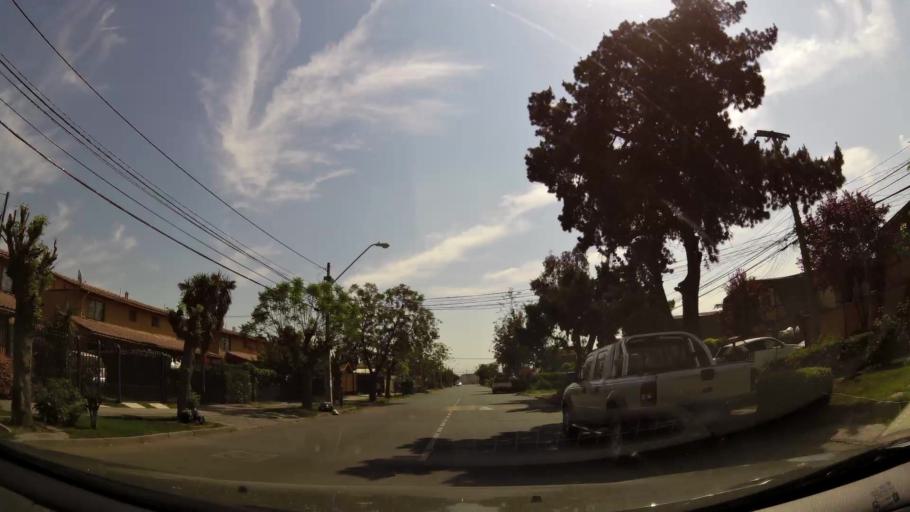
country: CL
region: Santiago Metropolitan
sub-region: Provincia de Cordillera
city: Puente Alto
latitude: -33.5795
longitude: -70.5927
